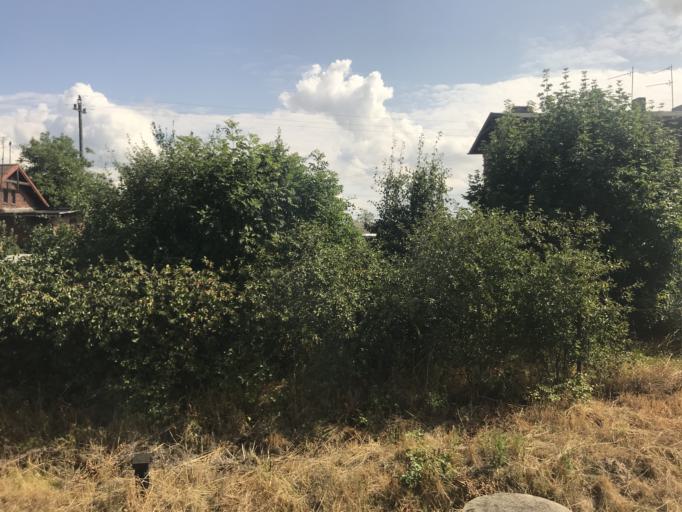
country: PL
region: Kujawsko-Pomorskie
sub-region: Powiat inowroclawski
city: Zlotniki Kujawskie
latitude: 52.9087
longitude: 18.1418
